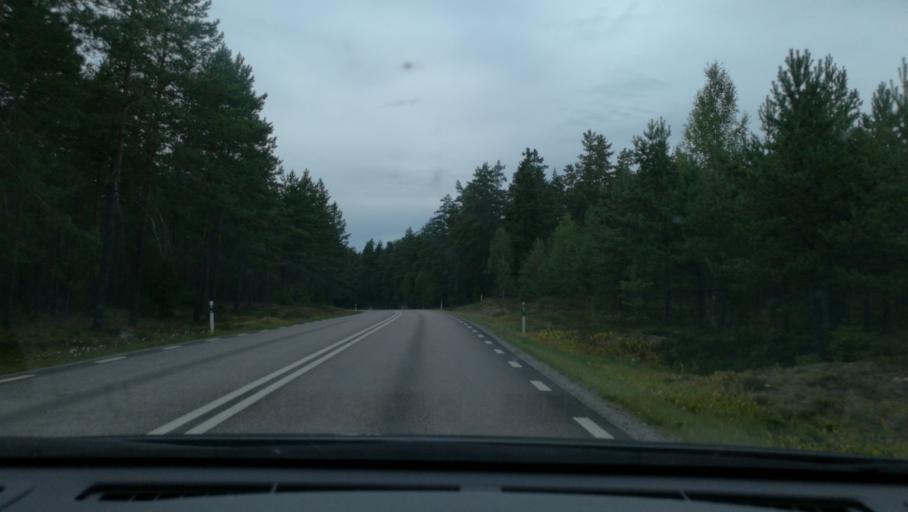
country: SE
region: Soedermanland
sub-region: Katrineholms Kommun
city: Katrineholm
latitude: 59.1085
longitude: 16.1768
